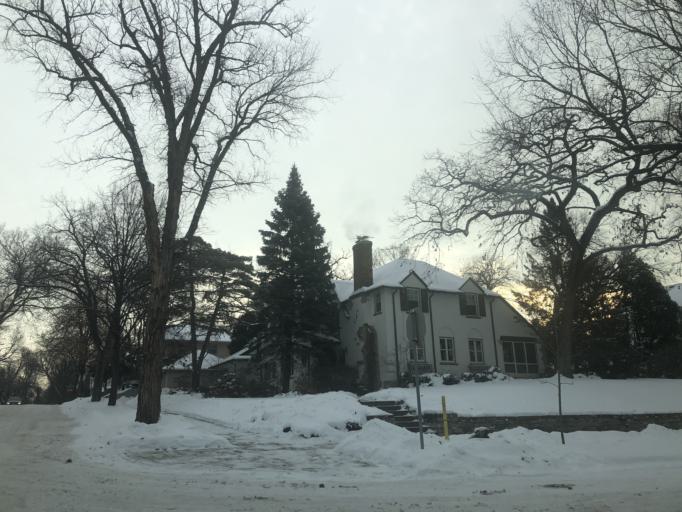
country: US
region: Minnesota
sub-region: Hennepin County
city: Richfield
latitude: 44.9178
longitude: -93.2973
